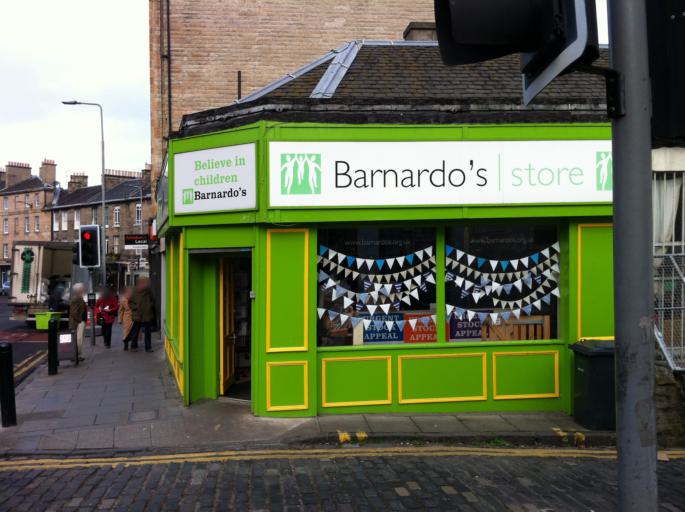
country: GB
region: Scotland
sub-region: Edinburgh
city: Edinburgh
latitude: 55.9584
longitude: -3.2094
